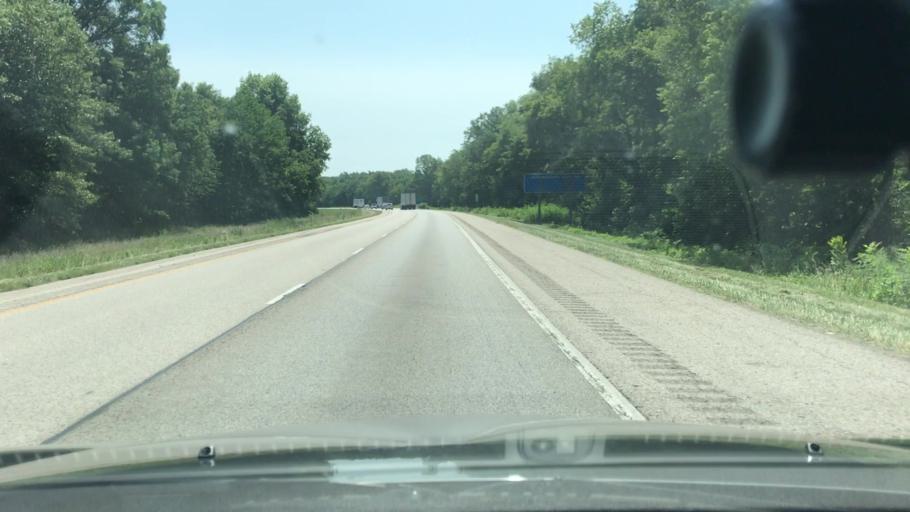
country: US
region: Illinois
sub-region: Washington County
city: Nashville
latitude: 38.4034
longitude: -89.4050
